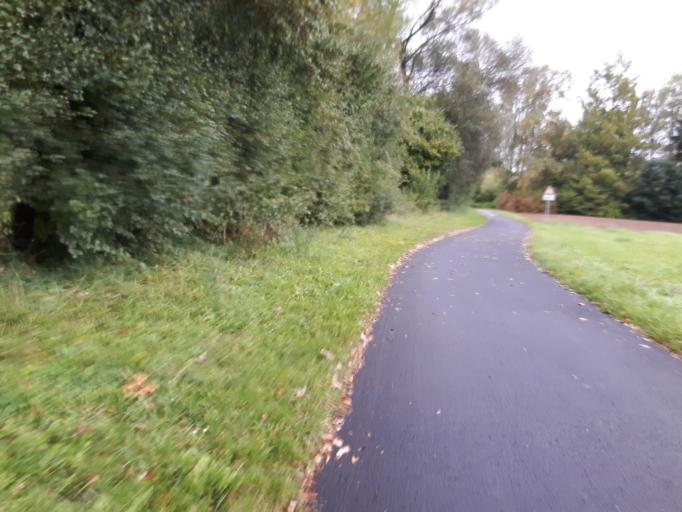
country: DE
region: Bavaria
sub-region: Regierungsbezirk Unterfranken
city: Thungersheim
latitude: 49.8771
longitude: 9.8369
